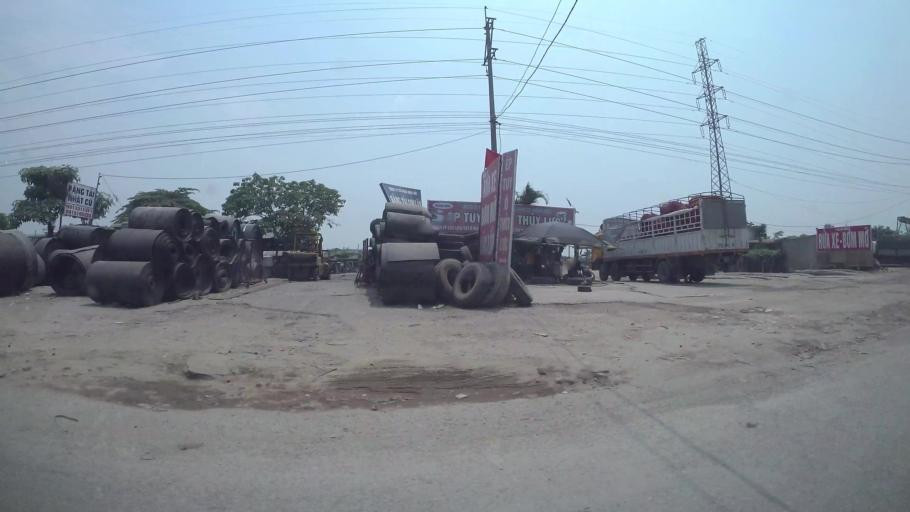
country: VN
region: Ha Noi
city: Van Dien
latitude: 20.9439
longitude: 105.8384
